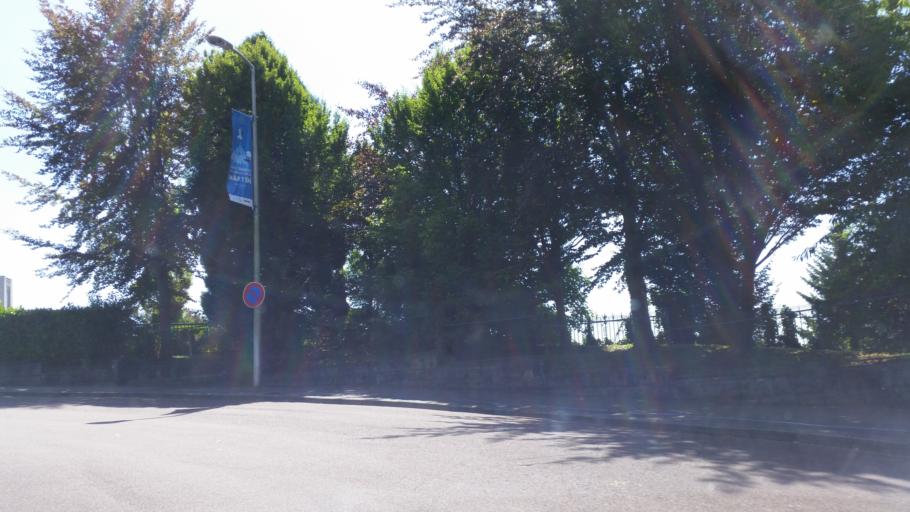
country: FR
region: Lower Normandy
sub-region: Departement du Calvados
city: Lisieux
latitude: 49.1413
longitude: 0.2333
